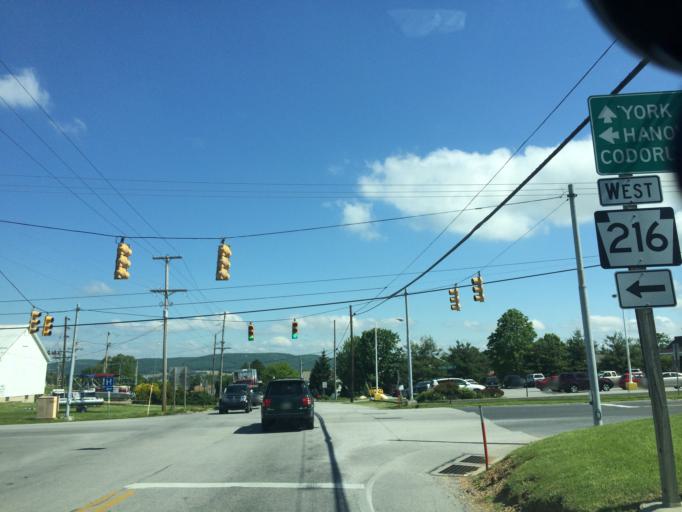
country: US
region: Pennsylvania
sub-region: York County
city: Parkville
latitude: 39.7946
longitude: -76.9443
